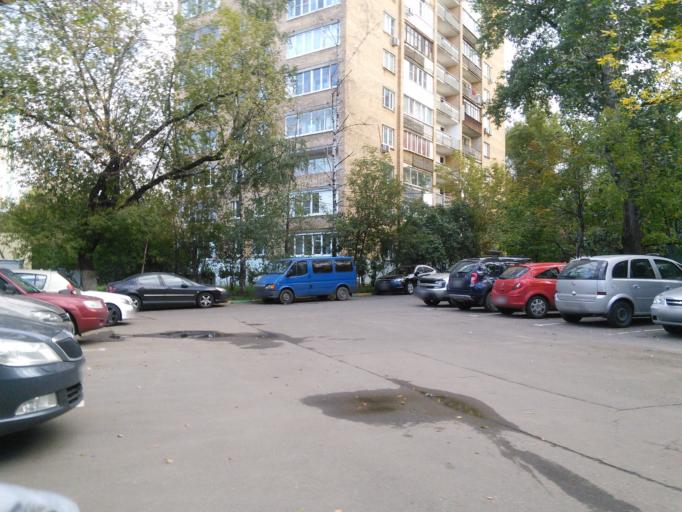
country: RU
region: Moskovskaya
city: Leninskiye Gory
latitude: 55.6968
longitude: 37.5713
